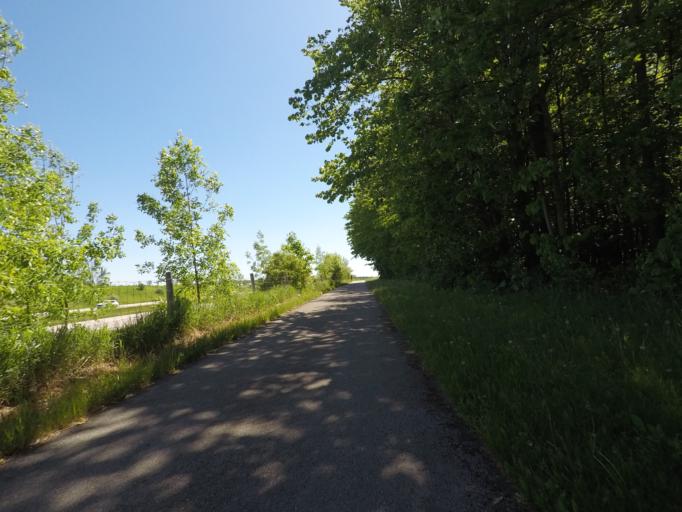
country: US
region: Wisconsin
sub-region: Sheboygan County
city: Sheboygan Falls
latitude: 43.7501
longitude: -87.8093
